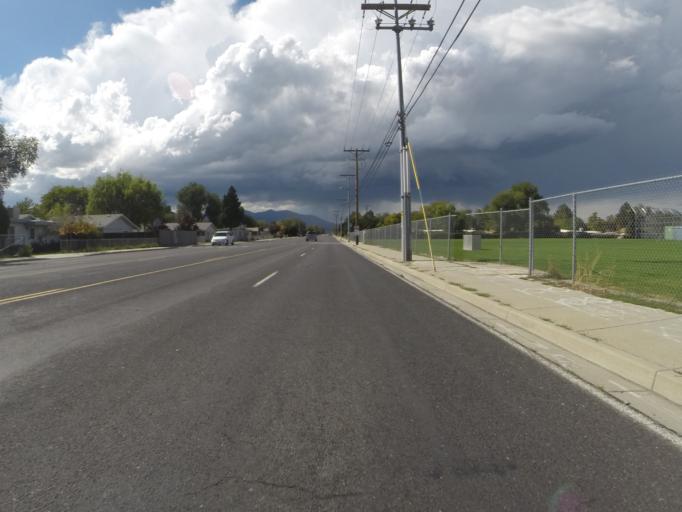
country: US
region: Utah
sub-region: Salt Lake County
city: Taylorsville
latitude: 40.7040
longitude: -111.9592
